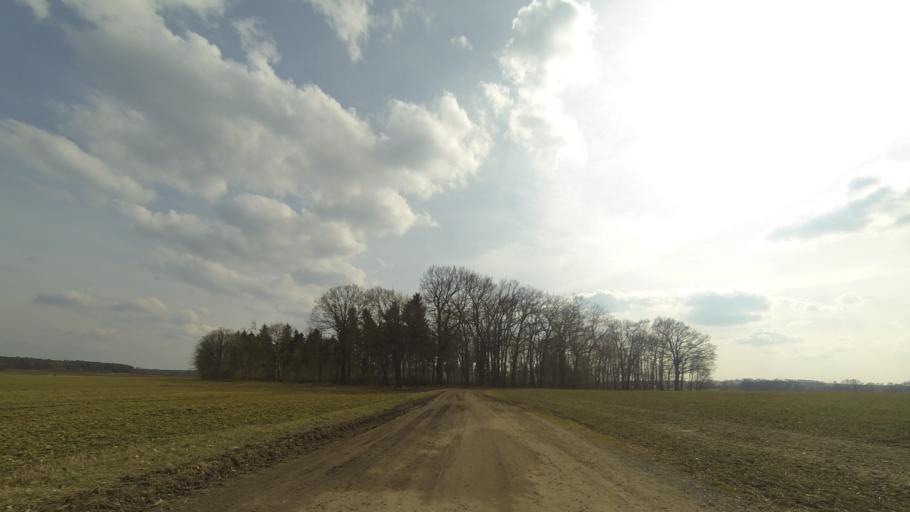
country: DE
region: Saxony
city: Radeburg
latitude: 51.2511
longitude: 13.7045
